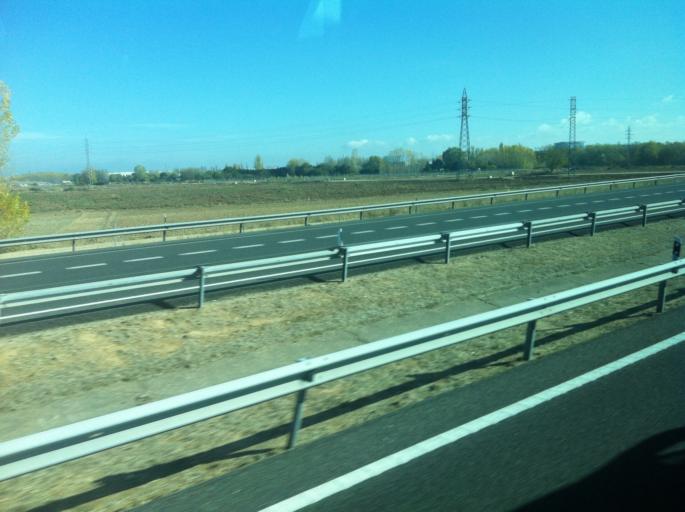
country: ES
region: Castille and Leon
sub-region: Provincia de Burgos
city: Villalba de Duero
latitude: 41.6716
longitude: -3.7289
